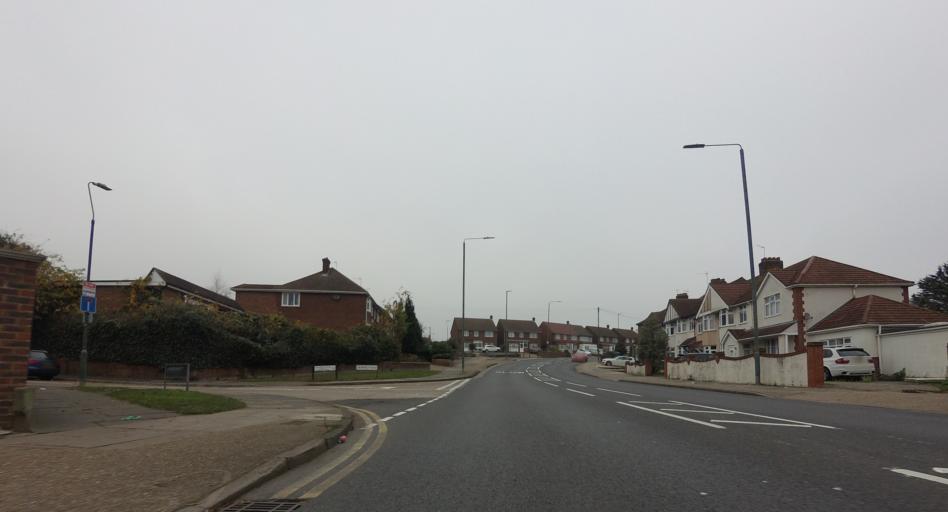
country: GB
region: England
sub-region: Greater London
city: Sidcup
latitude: 51.4409
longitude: 0.1175
